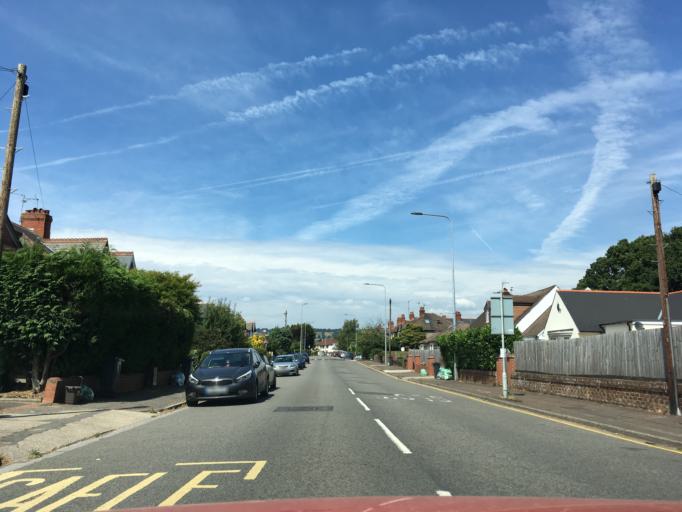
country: GB
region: Wales
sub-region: Cardiff
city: Cardiff
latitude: 51.5141
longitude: -3.1824
